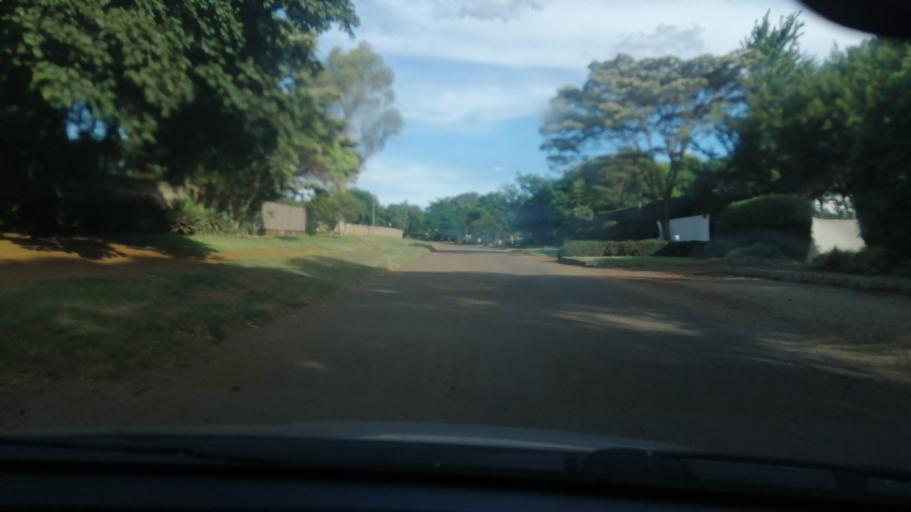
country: ZW
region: Harare
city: Harare
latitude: -17.7641
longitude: 31.0676
